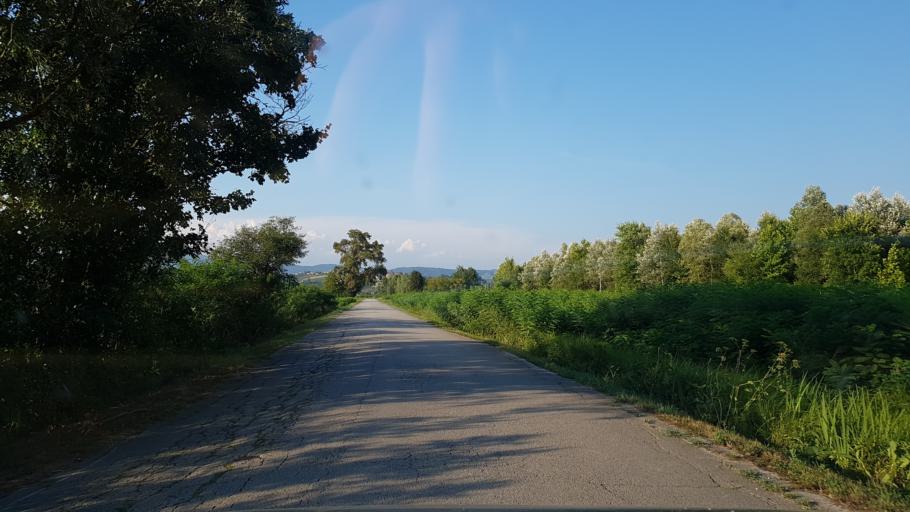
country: IT
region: Friuli Venezia Giulia
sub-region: Provincia di Gorizia
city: Capriva del Friuli
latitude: 45.9566
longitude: 13.5208
